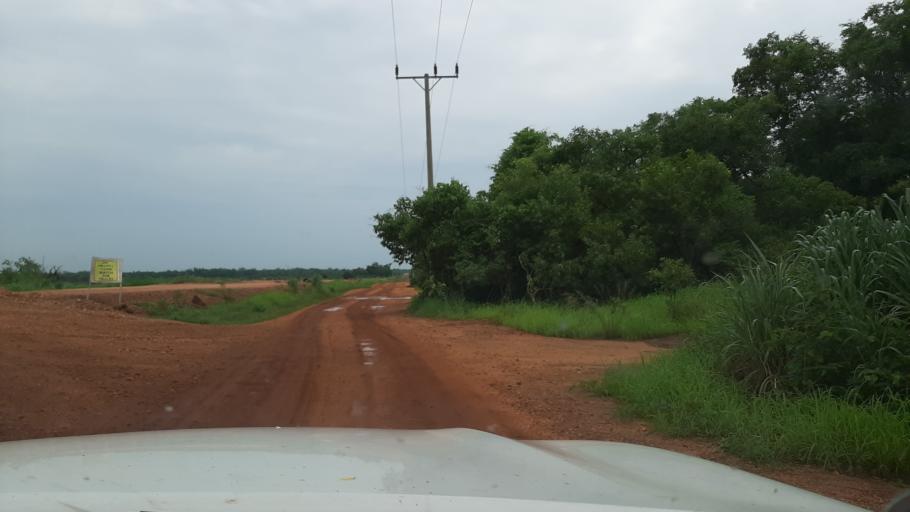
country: ET
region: Gambela
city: Gambela
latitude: 8.1549
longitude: 34.3060
